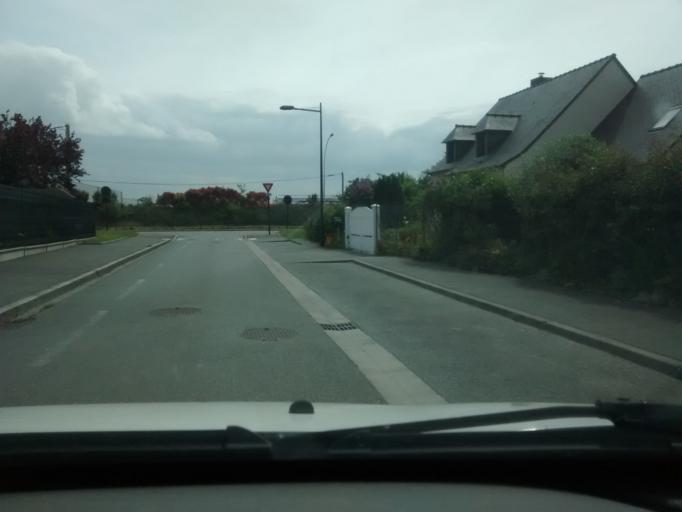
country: FR
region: Brittany
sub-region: Departement d'Ille-et-Vilaine
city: Dinard
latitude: 48.6183
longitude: -2.0664
